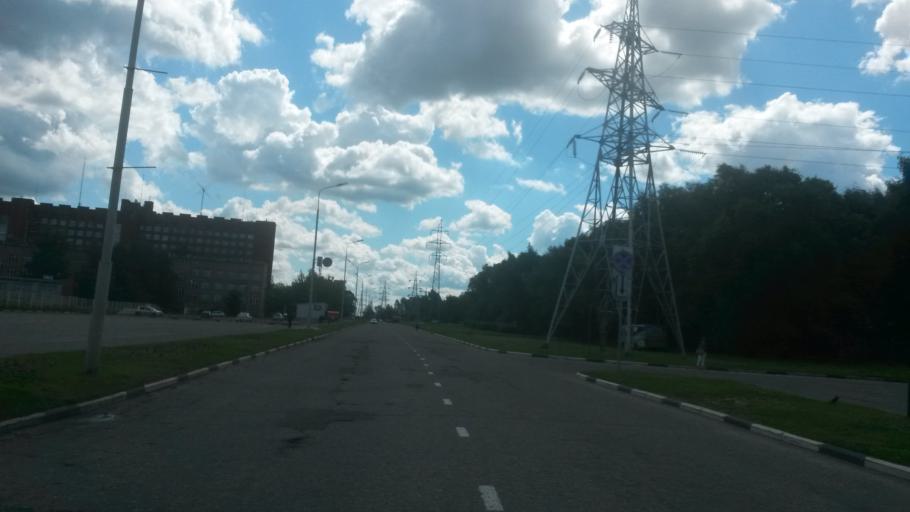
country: RU
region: Jaroslavl
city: Yaroslavl
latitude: 57.5873
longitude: 39.8495
